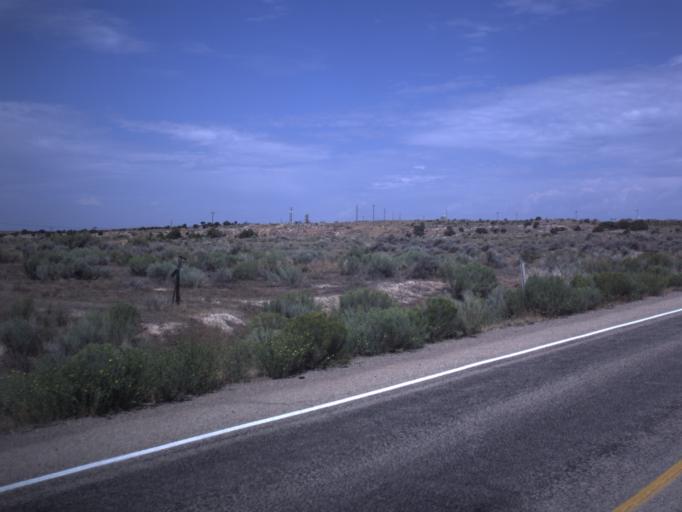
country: US
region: Utah
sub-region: Uintah County
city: Naples
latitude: 40.1793
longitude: -109.3236
